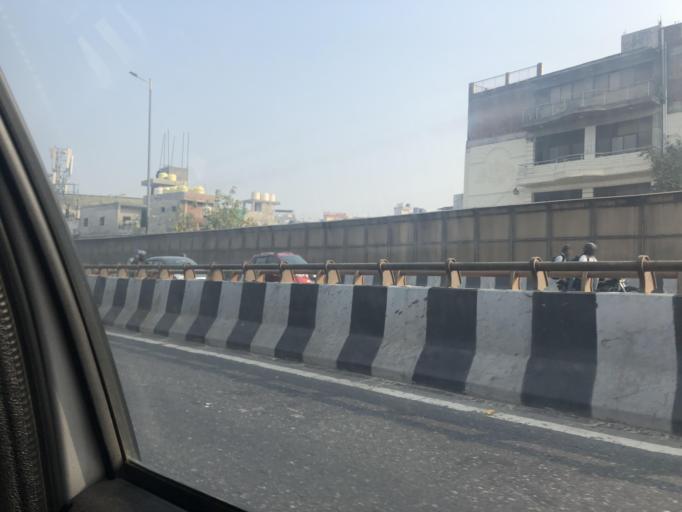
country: IN
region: NCT
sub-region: Central Delhi
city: Karol Bagh
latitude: 28.6197
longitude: 77.1364
